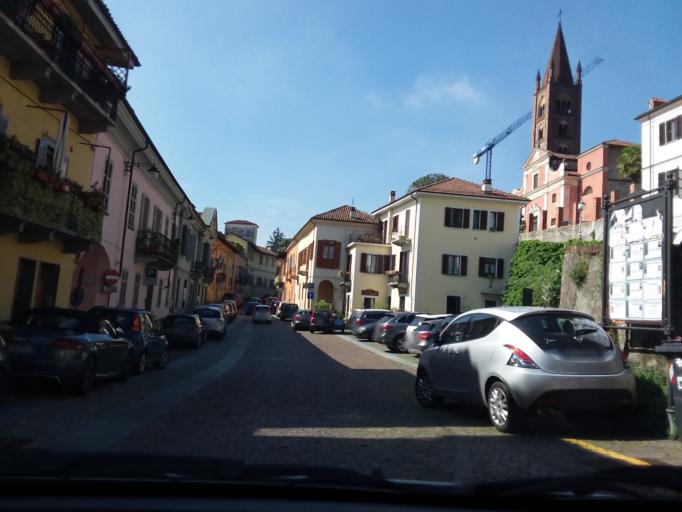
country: IT
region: Piedmont
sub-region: Provincia di Torino
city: Rivoli
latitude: 45.0704
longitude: 7.5128
